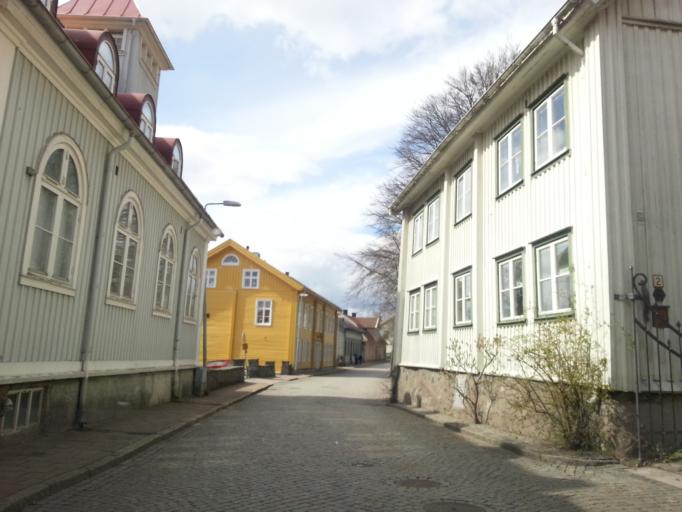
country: SE
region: Vaestra Goetaland
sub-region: Kungalvs Kommun
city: Kungalv
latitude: 57.8657
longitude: 11.9942
